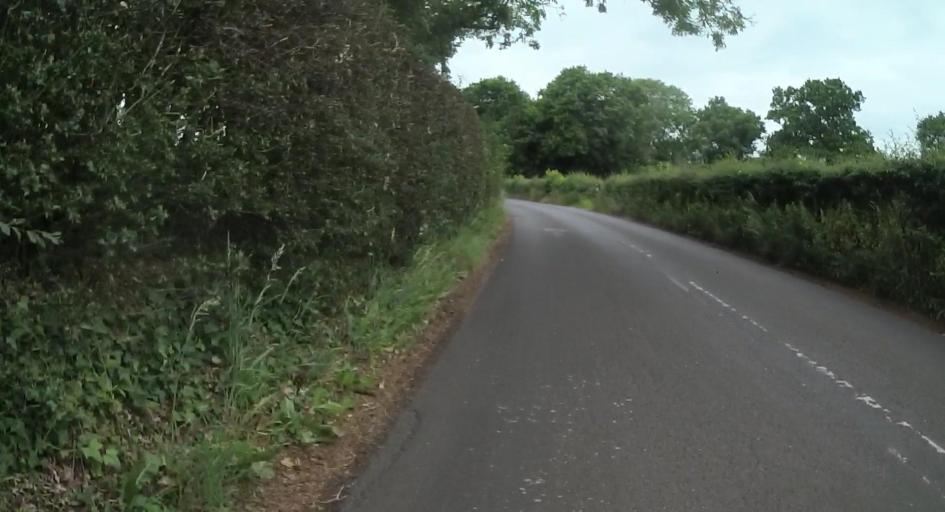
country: GB
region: England
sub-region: Surrey
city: Churt
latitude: 51.1651
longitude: -0.8005
